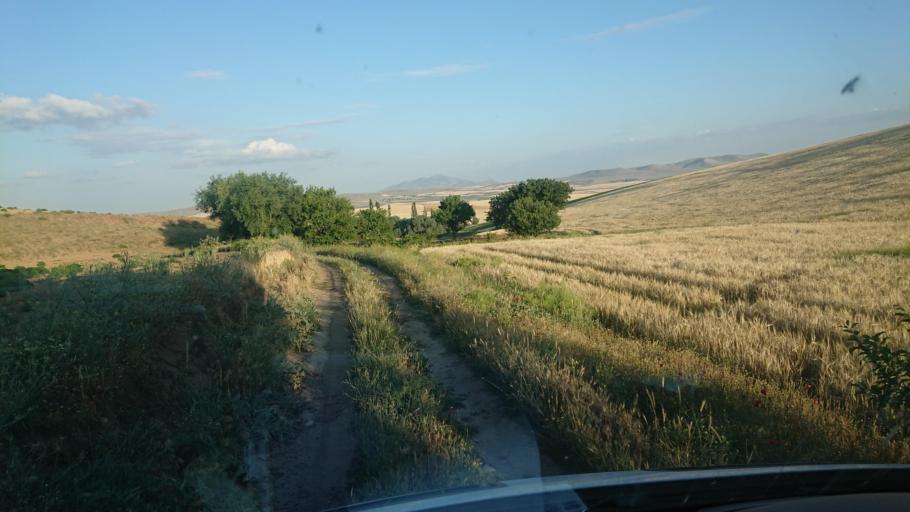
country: TR
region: Aksaray
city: Agacoren
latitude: 38.8318
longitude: 33.8850
